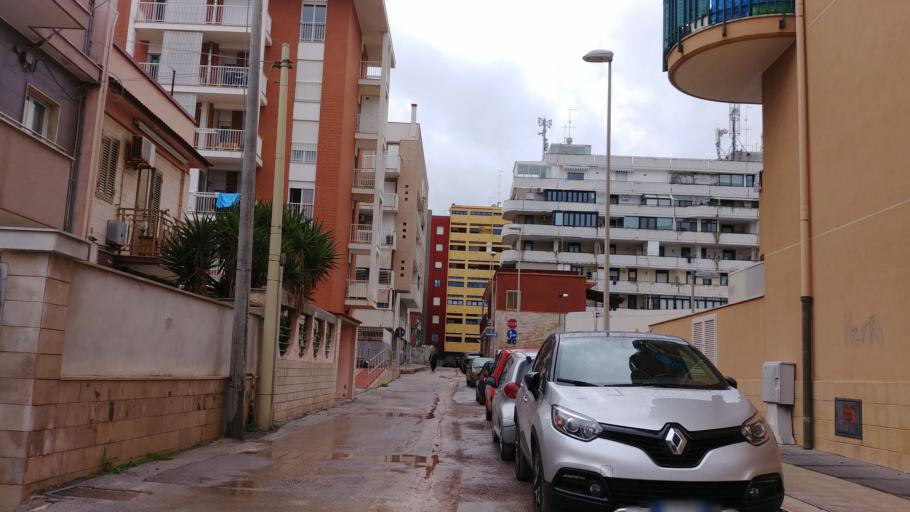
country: IT
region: Apulia
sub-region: Provincia di Bari
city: San Paolo
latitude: 41.1393
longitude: 16.8149
